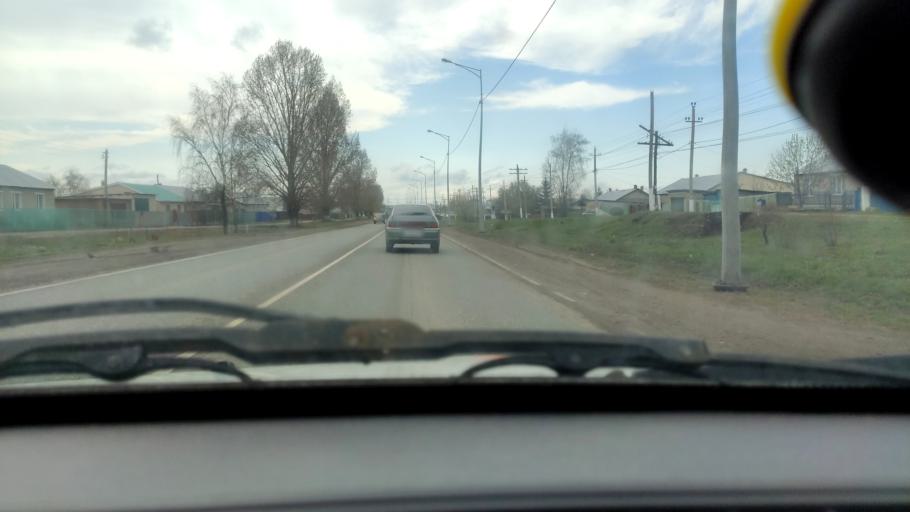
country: RU
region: Samara
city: Zhigulevsk
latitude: 53.5540
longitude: 49.5312
